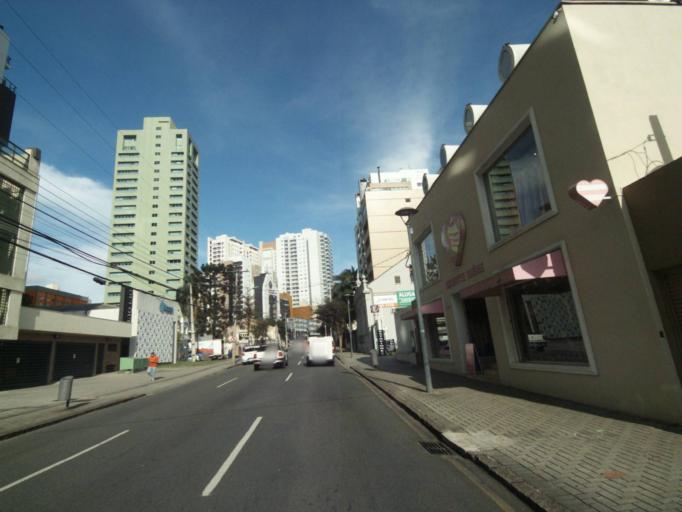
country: BR
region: Parana
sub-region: Curitiba
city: Curitiba
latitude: -25.4377
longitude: -49.2804
